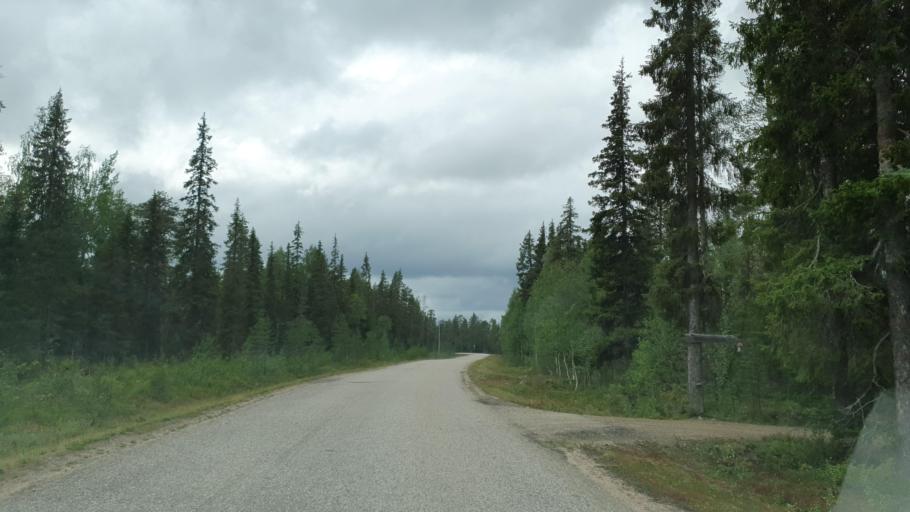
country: FI
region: Lapland
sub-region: Tunturi-Lappi
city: Kolari
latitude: 67.5214
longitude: 24.1820
